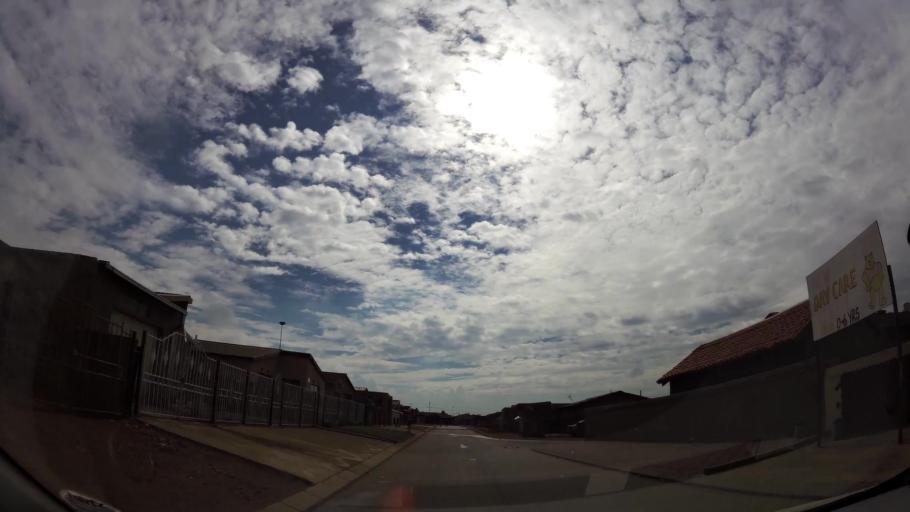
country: ZA
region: Gauteng
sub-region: Ekurhuleni Metropolitan Municipality
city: Germiston
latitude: -26.3735
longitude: 28.1642
